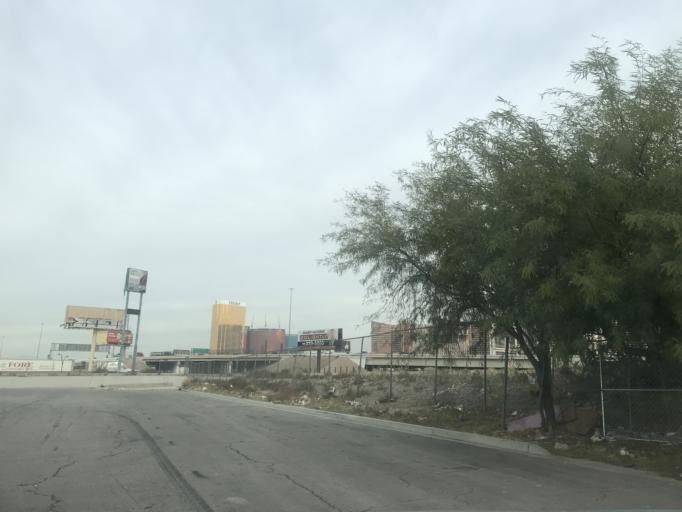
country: US
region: Nevada
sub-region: Clark County
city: Paradise
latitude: 36.1194
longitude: -115.1827
